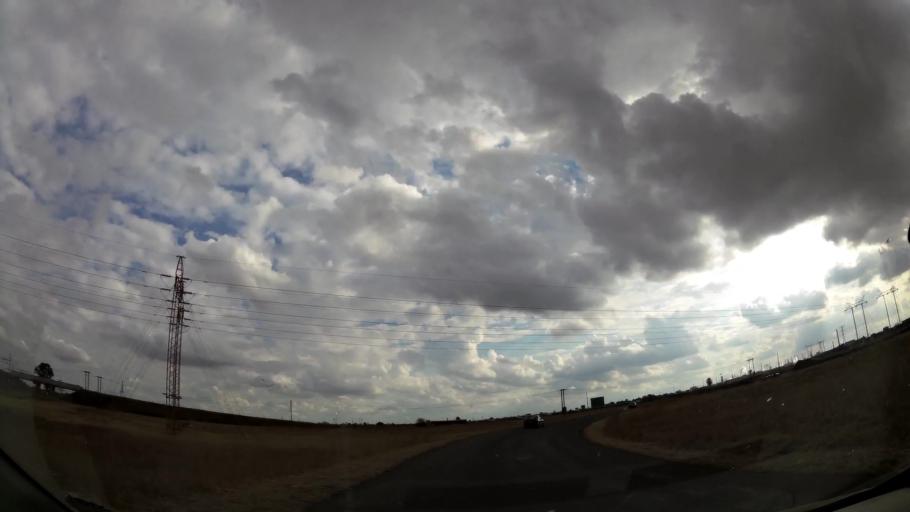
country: ZA
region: Orange Free State
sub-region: Fezile Dabi District Municipality
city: Sasolburg
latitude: -26.8405
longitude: 27.8746
